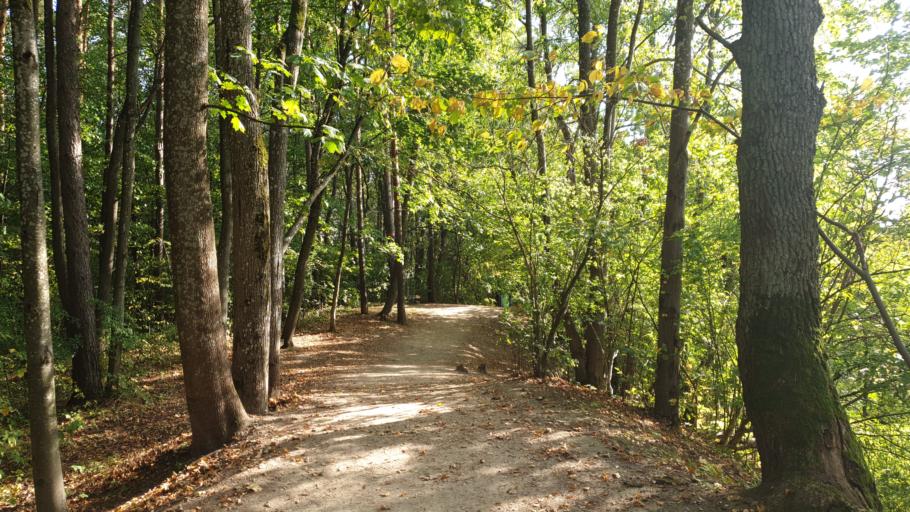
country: LT
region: Vilnius County
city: Rasos
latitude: 54.6921
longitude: 25.3538
